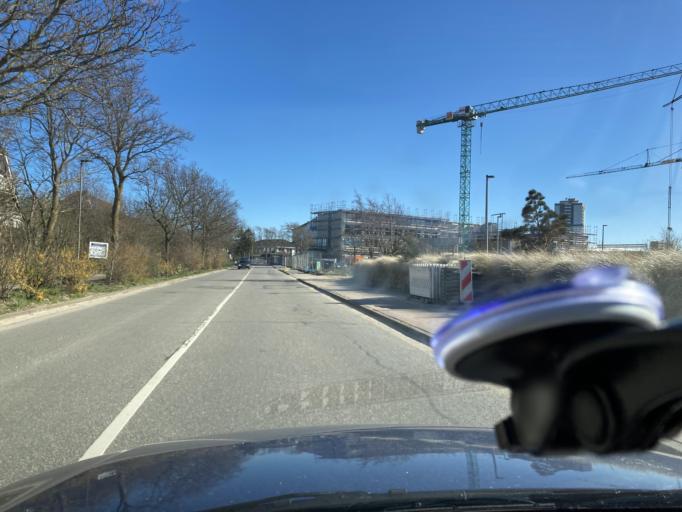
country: DE
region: Schleswig-Holstein
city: Busum
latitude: 54.1366
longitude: 8.8452
